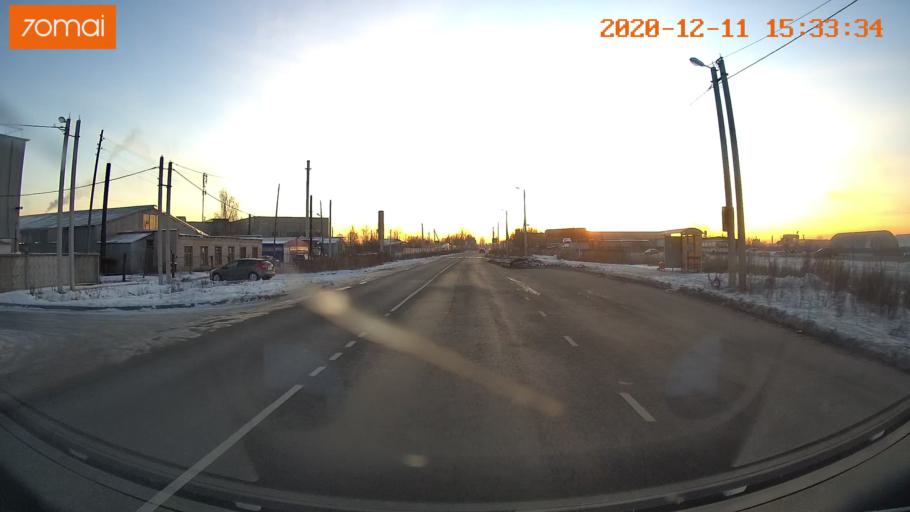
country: RU
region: Ivanovo
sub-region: Gorod Ivanovo
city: Ivanovo
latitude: 57.0507
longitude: 40.9466
